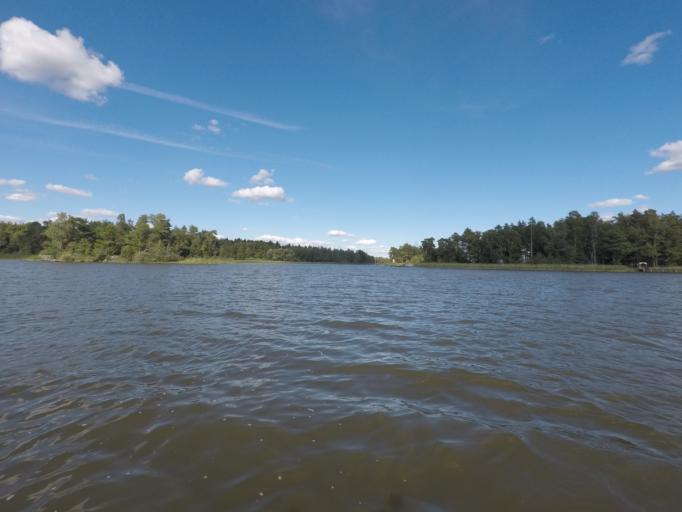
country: SE
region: Soedermanland
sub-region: Eskilstuna Kommun
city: Torshalla
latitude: 59.4781
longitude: 16.4513
